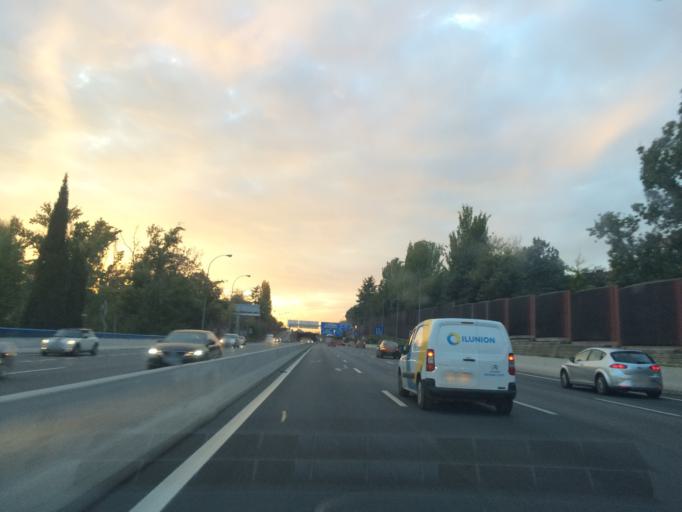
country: ES
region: Madrid
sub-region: Provincia de Madrid
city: Fuencarral-El Pardo
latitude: 40.4745
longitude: -3.7426
